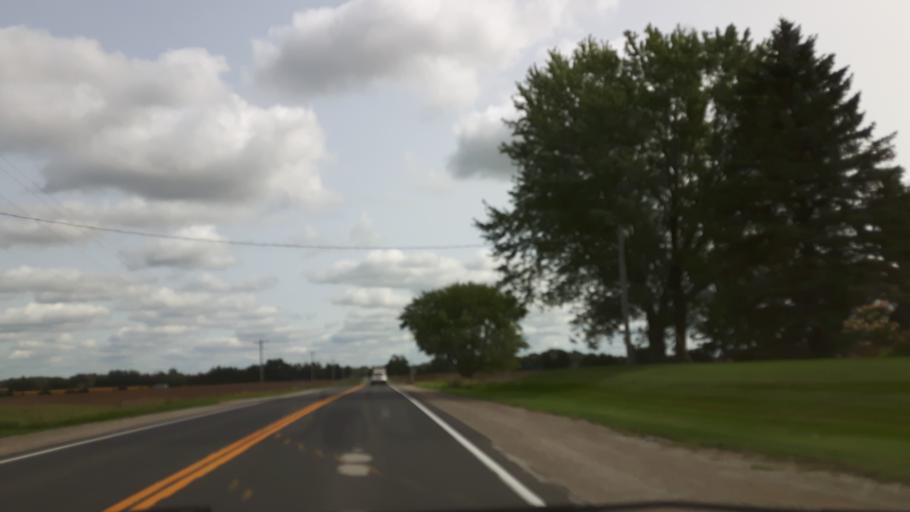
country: CA
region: Ontario
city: Huron East
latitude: 43.5678
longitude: -81.4263
